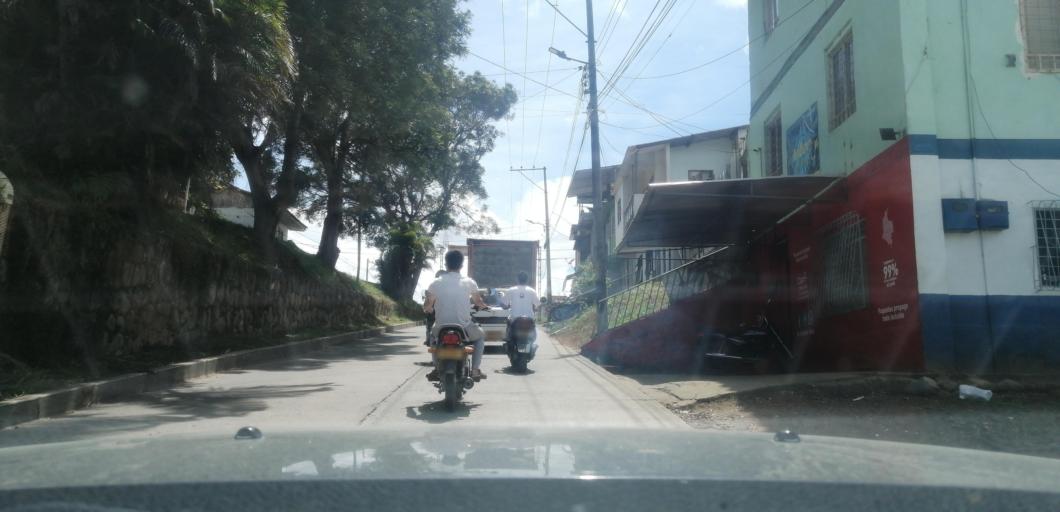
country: CO
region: Valle del Cauca
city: Restrepo
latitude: 3.8246
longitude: -76.5220
